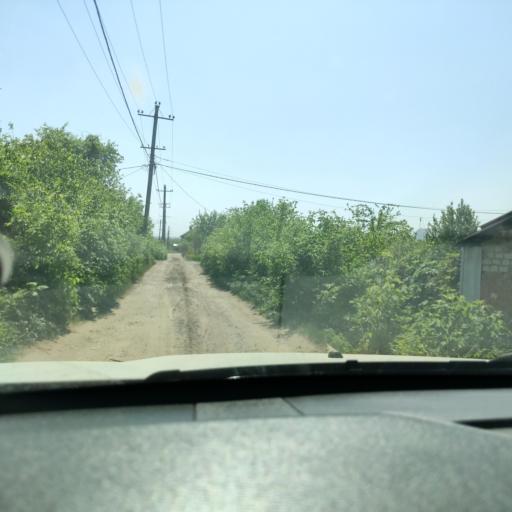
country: RU
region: Samara
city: Petra-Dubrava
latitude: 53.2767
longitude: 50.3286
